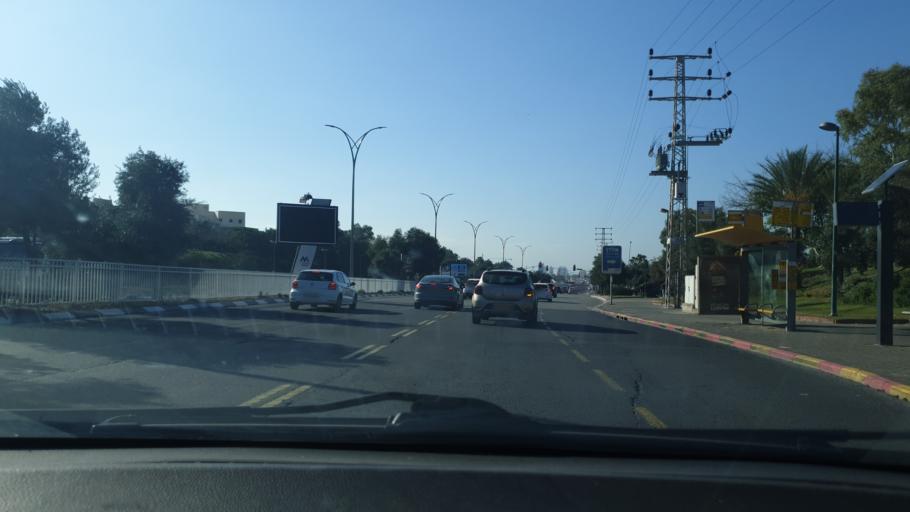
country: IL
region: Central District
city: Rishon LeZiyyon
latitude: 31.9806
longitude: 34.7752
